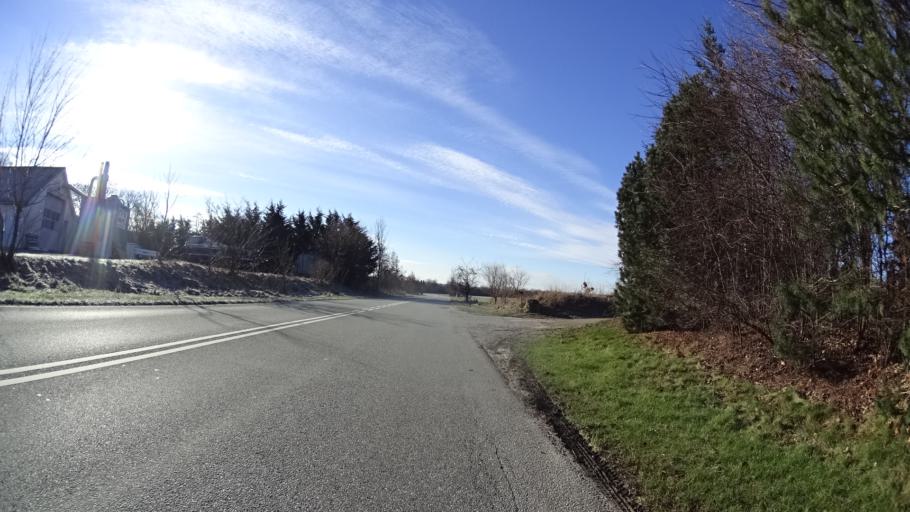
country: DK
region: Central Jutland
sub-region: Arhus Kommune
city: Kolt
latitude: 56.1111
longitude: 10.0703
